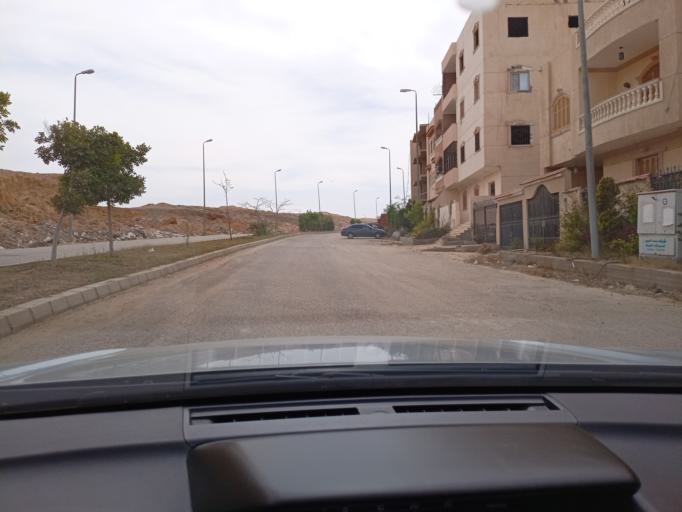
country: EG
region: Muhafazat al Qalyubiyah
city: Al Khankah
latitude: 30.2437
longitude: 31.4962
